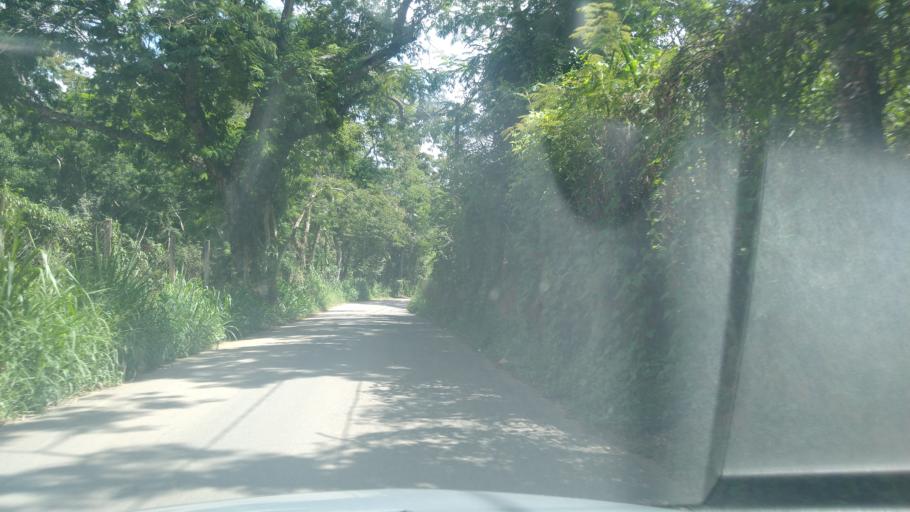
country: BR
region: Minas Gerais
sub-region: Extrema
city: Extrema
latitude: -22.7814
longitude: -46.2872
